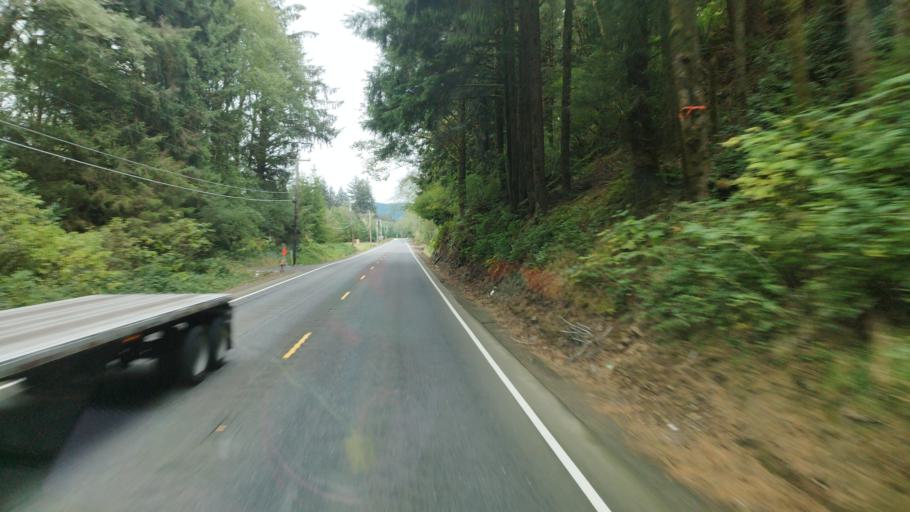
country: US
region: Oregon
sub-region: Clatsop County
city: Cannon Beach
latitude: 45.9172
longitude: -123.8924
